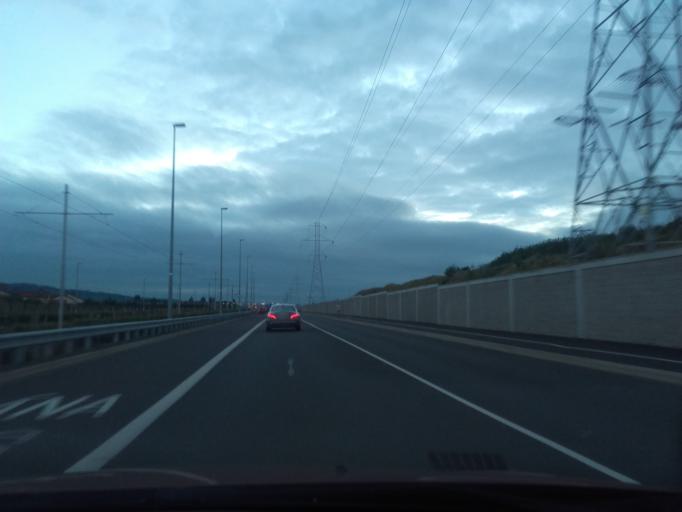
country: IE
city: Jobstown
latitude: 53.2926
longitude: -6.4003
